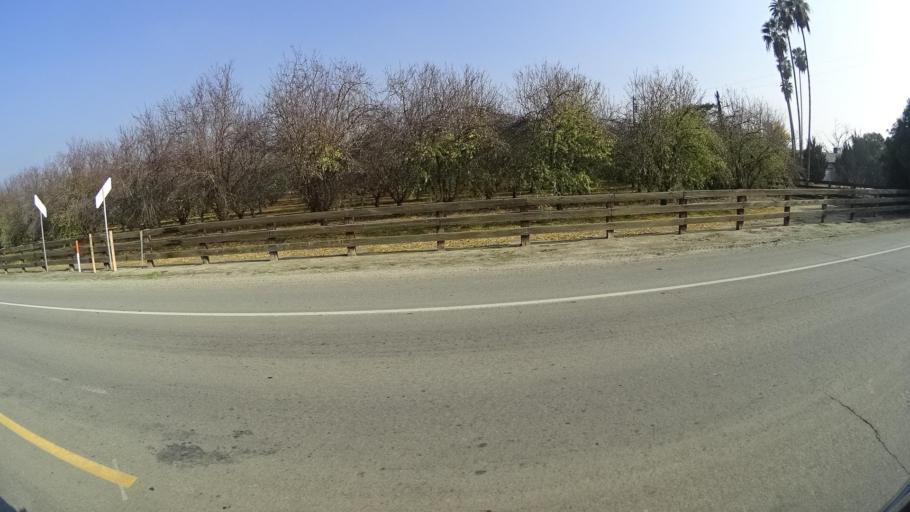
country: US
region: California
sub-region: Kern County
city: Greenfield
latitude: 35.2280
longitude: -119.1099
